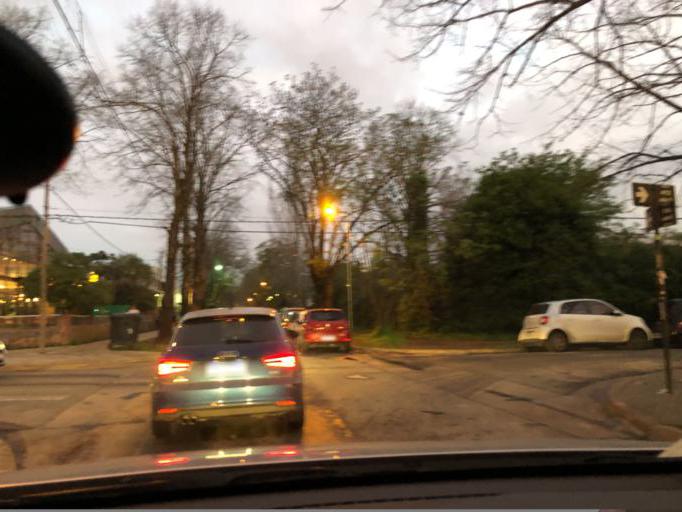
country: AR
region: Buenos Aires
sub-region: Partido de La Plata
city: La Plata
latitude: -34.8680
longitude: -58.0457
